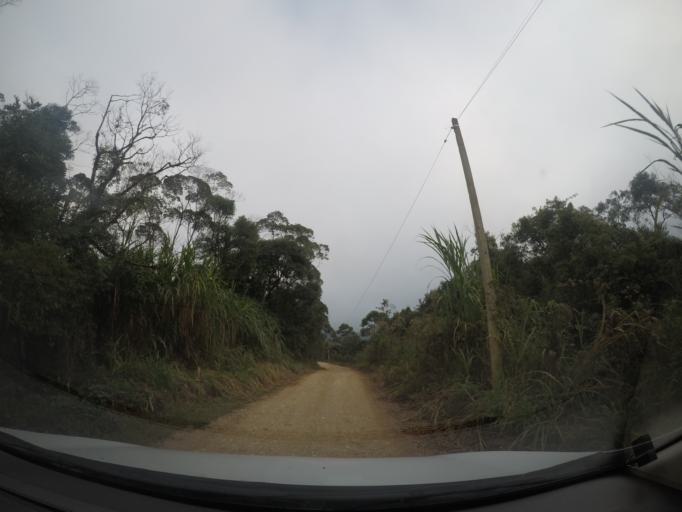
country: BR
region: Parana
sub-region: Colombo
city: Colombo
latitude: -25.3172
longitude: -49.2491
